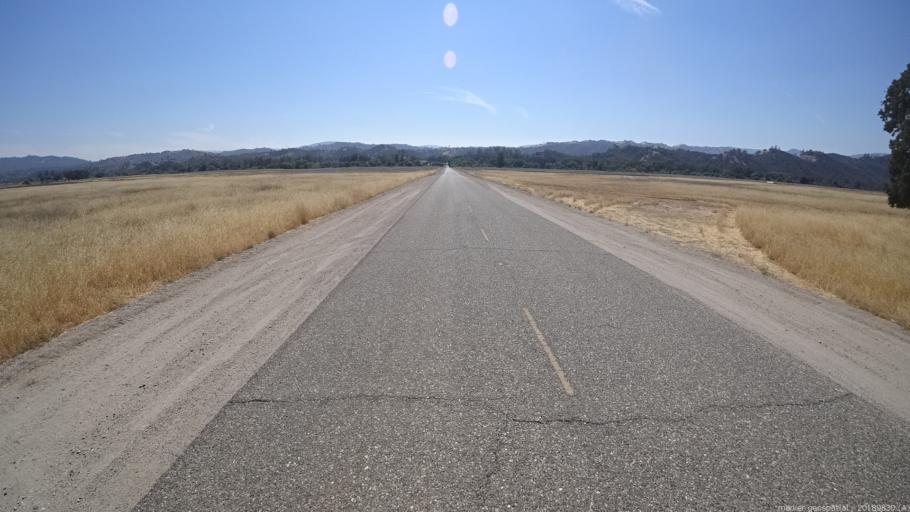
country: US
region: California
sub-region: Monterey County
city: King City
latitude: 36.0063
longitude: -121.2437
